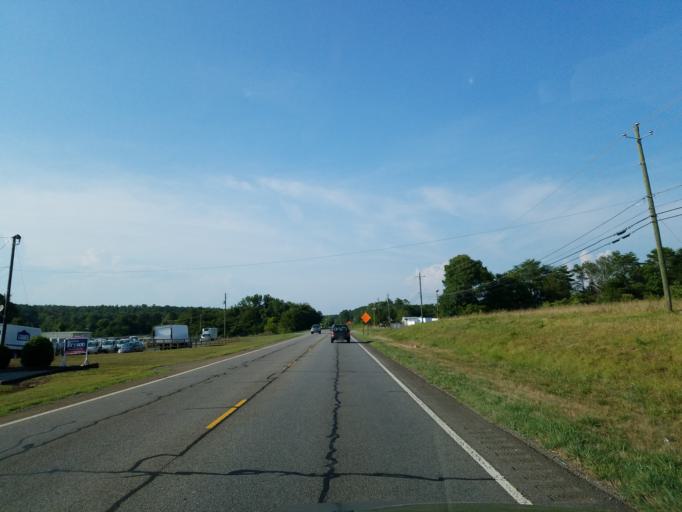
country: US
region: Georgia
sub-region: Bartow County
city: Rydal
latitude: 34.3262
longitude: -84.7178
